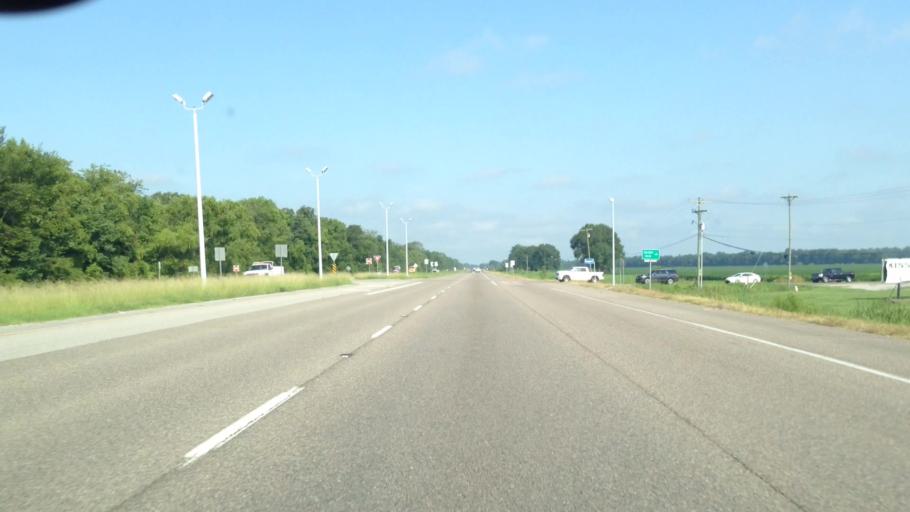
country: US
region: Louisiana
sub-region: West Baton Rouge Parish
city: Erwinville
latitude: 30.5185
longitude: -91.3634
